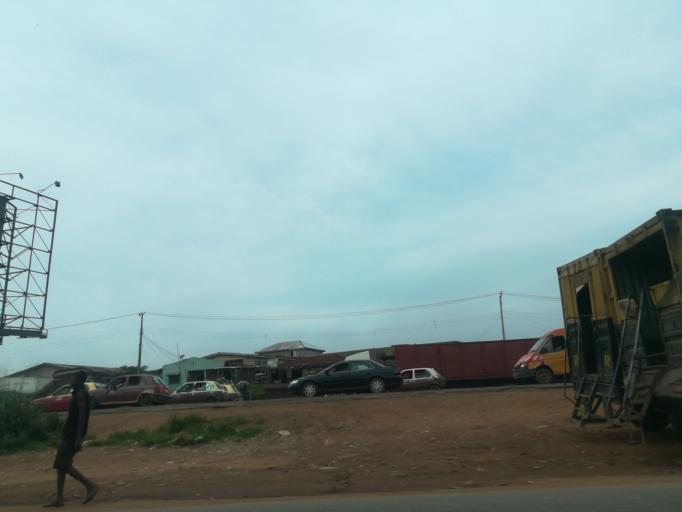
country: NG
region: Oyo
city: Ibadan
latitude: 7.3728
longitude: 3.9300
